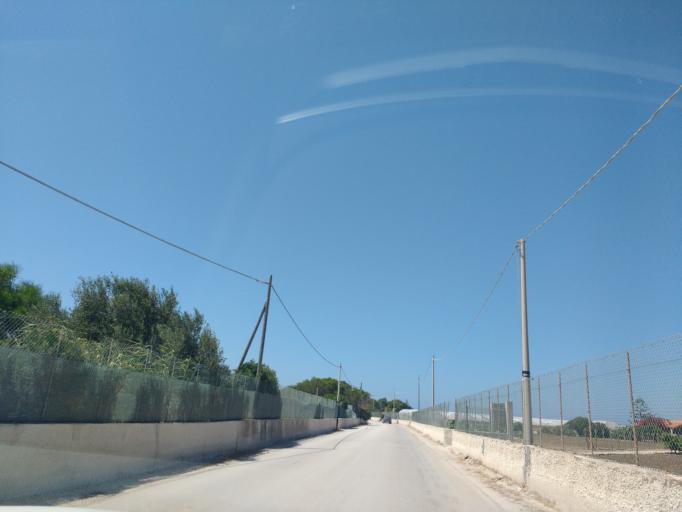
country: IT
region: Sicily
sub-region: Provincia di Siracusa
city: Portopalo di Capo Passero
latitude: 36.6589
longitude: 15.0801
